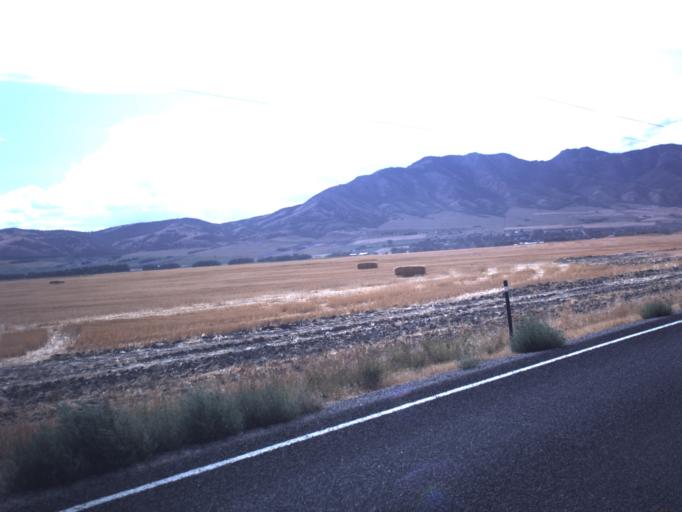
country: US
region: Utah
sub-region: Cache County
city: Benson
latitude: 41.9177
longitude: -112.0023
